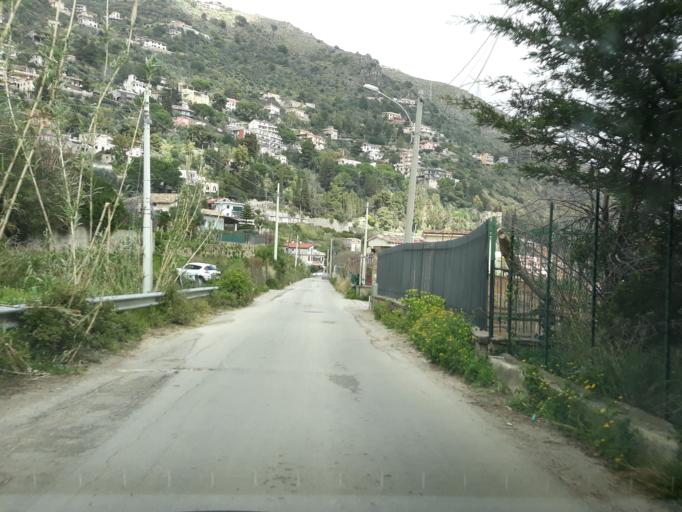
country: IT
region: Sicily
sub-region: Palermo
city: Monreale
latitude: 38.0839
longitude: 13.2980
